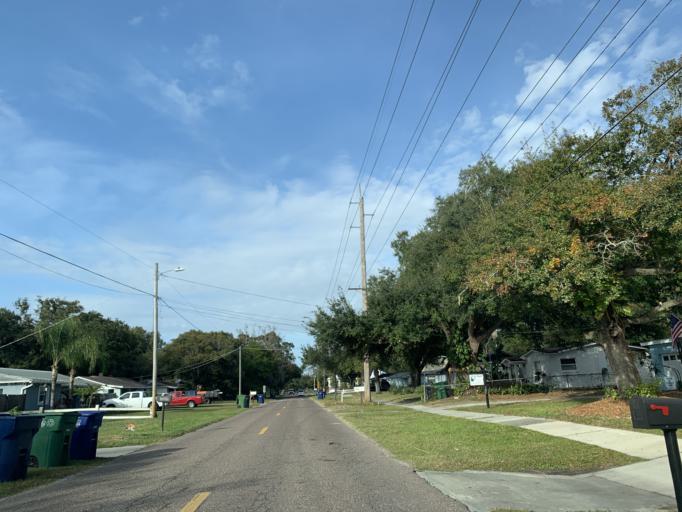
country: US
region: Florida
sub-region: Hillsborough County
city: Tampa
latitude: 27.9027
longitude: -82.5123
